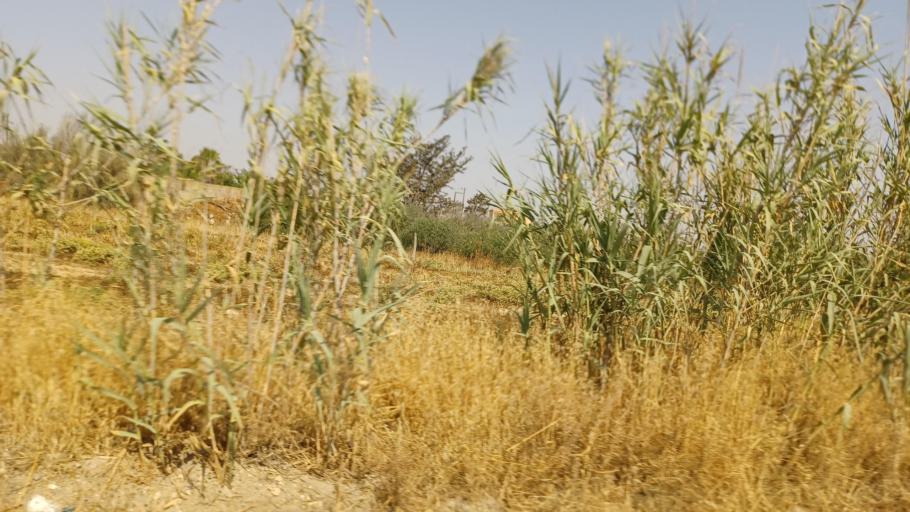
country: CY
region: Ammochostos
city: Avgorou
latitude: 35.0421
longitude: 33.8495
